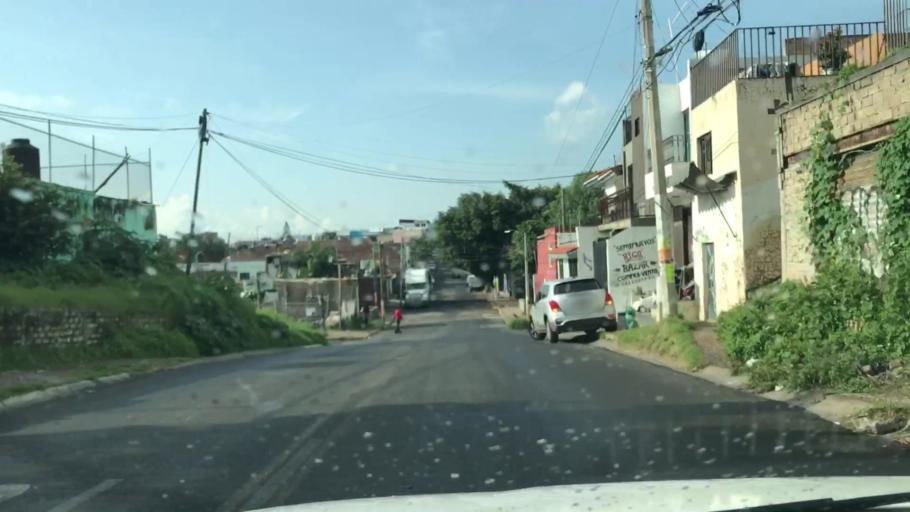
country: MX
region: Jalisco
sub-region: Tlajomulco de Zuniga
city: Palomar
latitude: 20.6372
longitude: -103.4535
